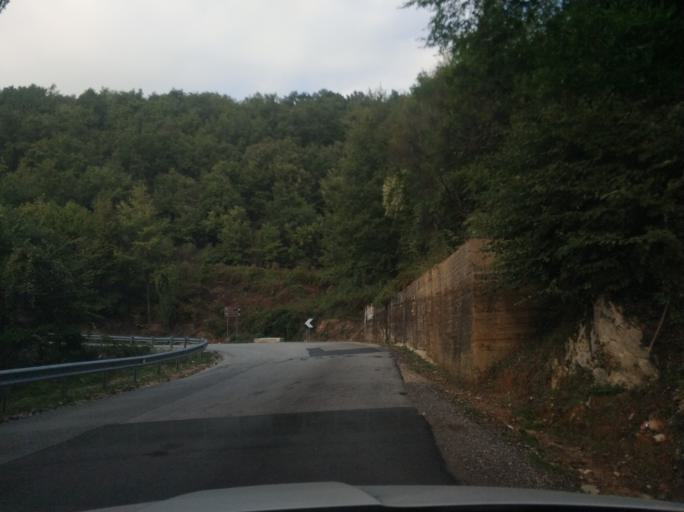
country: AL
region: Vlore
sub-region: Rrethi i Sarandes
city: Dhiver
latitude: 39.9183
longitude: 20.2012
